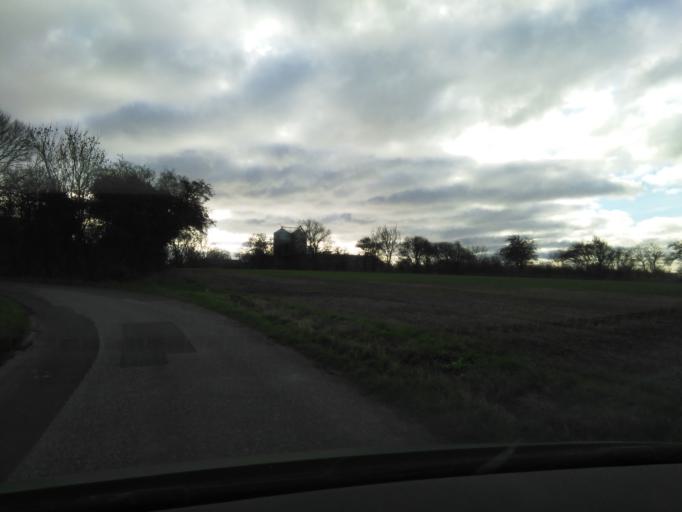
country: DK
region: Central Jutland
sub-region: Odder Kommune
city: Odder
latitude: 55.9080
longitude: 10.1872
